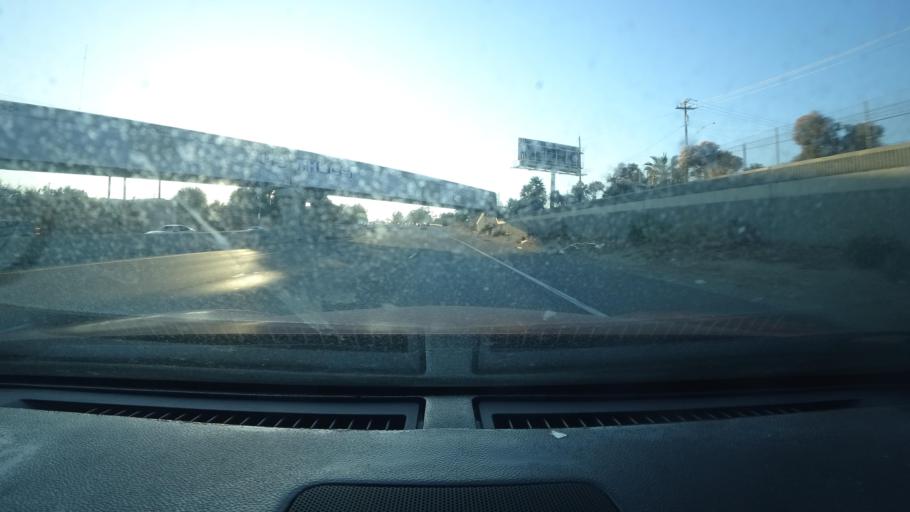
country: US
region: California
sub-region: Santa Clara County
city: San Jose
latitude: 37.3582
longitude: -121.8706
